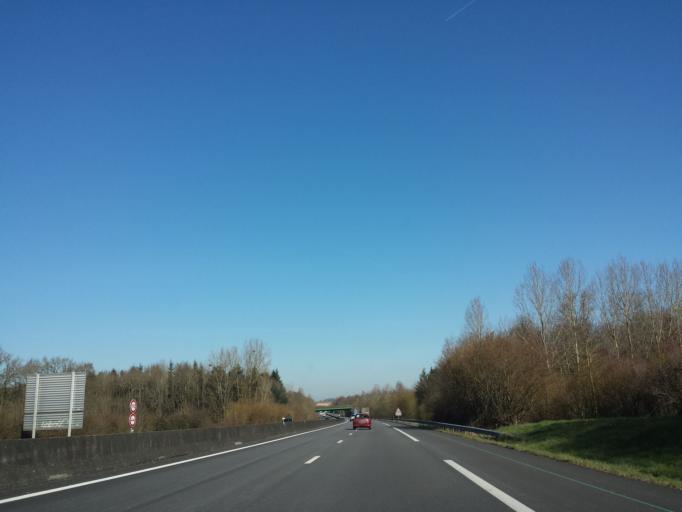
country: FR
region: Picardie
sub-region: Departement de l'Oise
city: Saint-Sulpice
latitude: 49.3490
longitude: 2.1080
